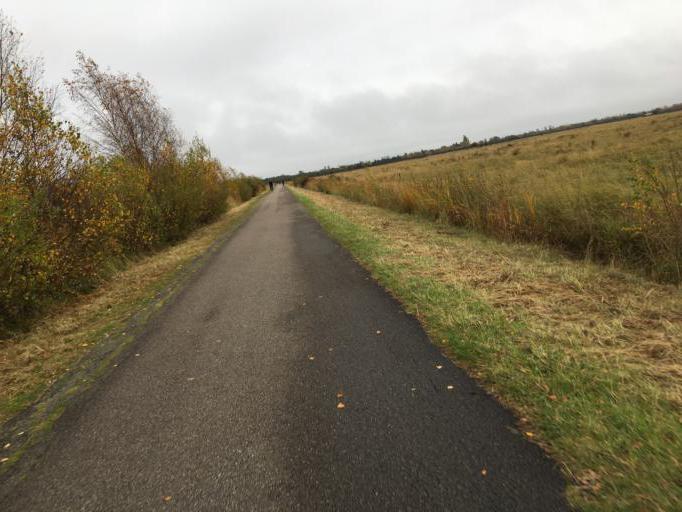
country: DK
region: Capital Region
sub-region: Tarnby Kommune
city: Tarnby
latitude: 55.6155
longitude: 12.5605
